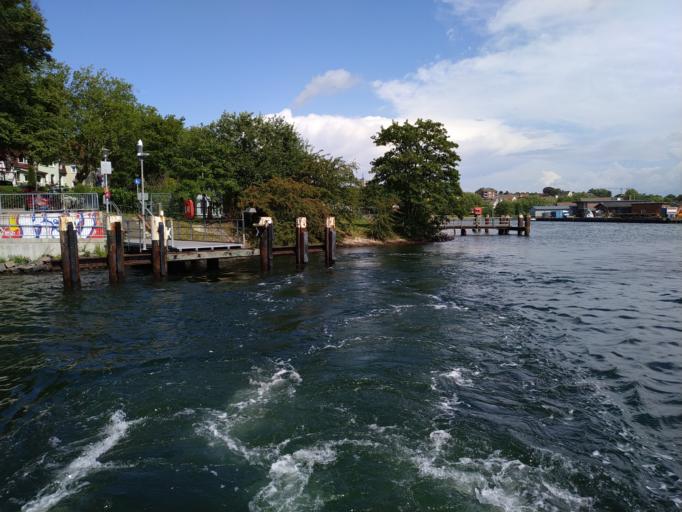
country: DE
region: Schleswig-Holstein
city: Altenholz
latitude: 54.3684
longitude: 10.1341
